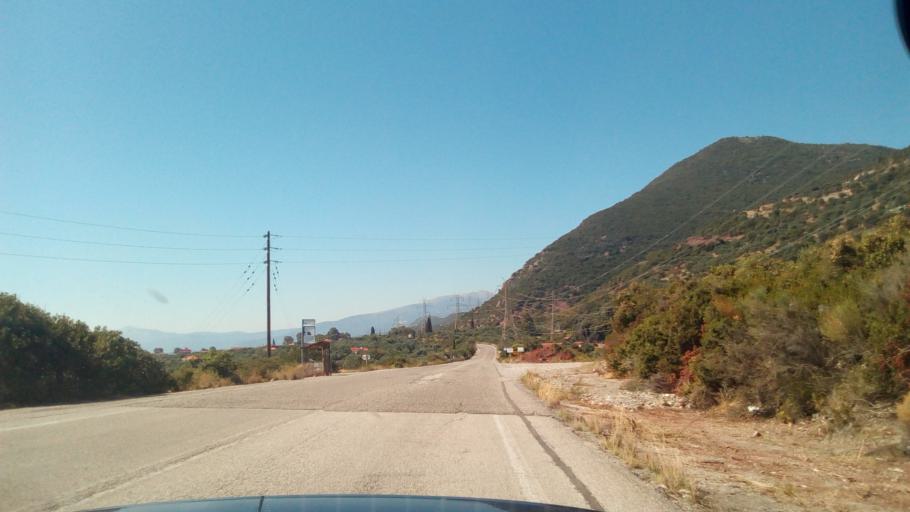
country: GR
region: West Greece
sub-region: Nomos Achaias
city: Kamarai
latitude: 38.3960
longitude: 22.0173
